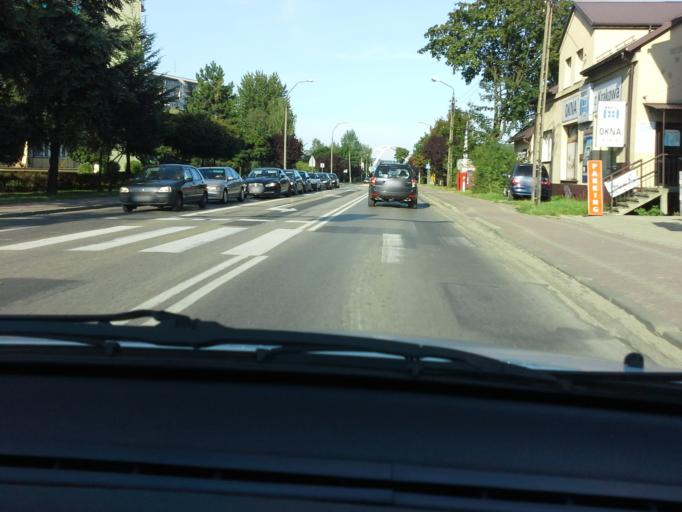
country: PL
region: Lesser Poland Voivodeship
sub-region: Powiat chrzanowski
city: Chrzanow
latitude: 50.1438
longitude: 19.4161
